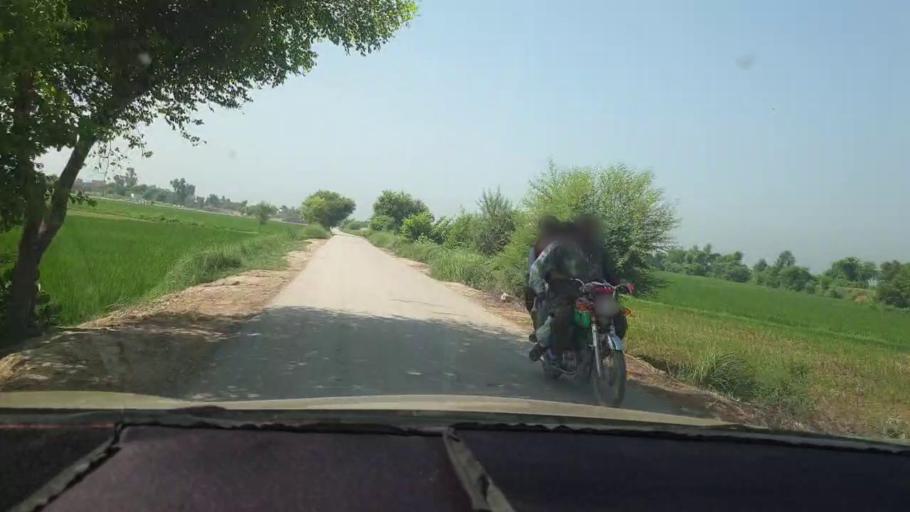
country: PK
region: Sindh
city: Kambar
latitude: 27.5756
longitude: 68.0430
